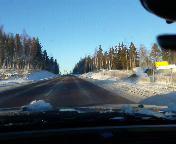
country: SE
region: Gaevleborg
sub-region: Ljusdals Kommun
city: Jaervsoe
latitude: 61.7663
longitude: 16.1576
